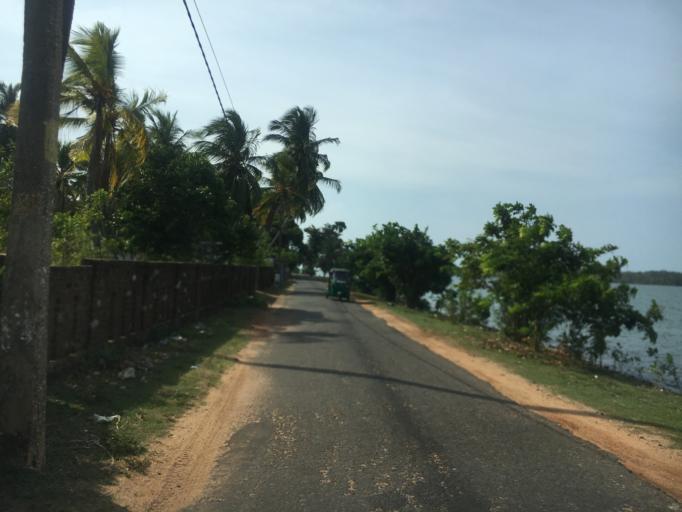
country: LK
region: Eastern Province
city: Batticaloa
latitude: 7.7411
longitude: 81.6956
